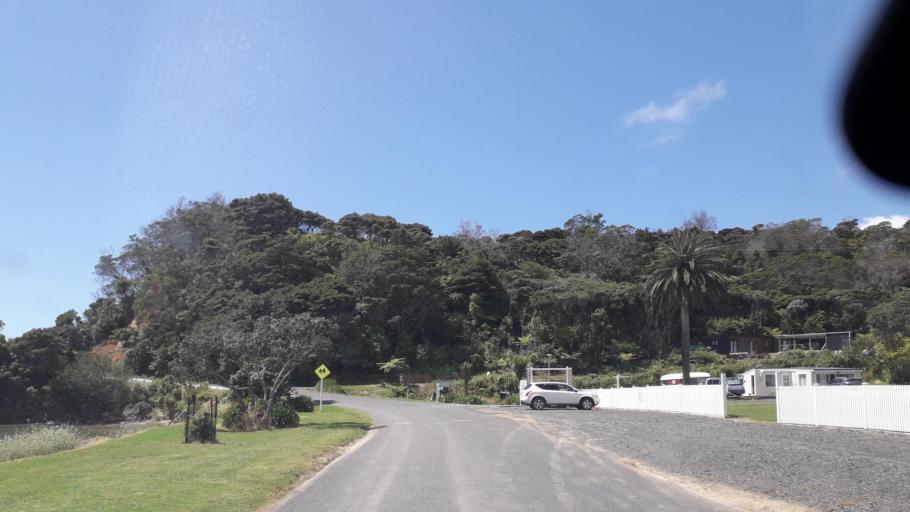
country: NZ
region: Northland
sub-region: Far North District
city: Paihia
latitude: -35.2362
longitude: 174.2602
